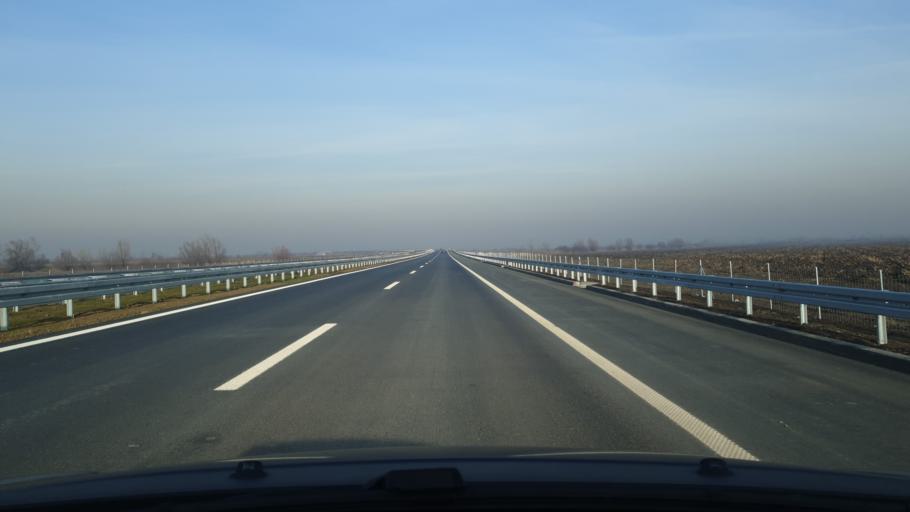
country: RS
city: Baric
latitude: 44.6796
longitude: 20.2602
